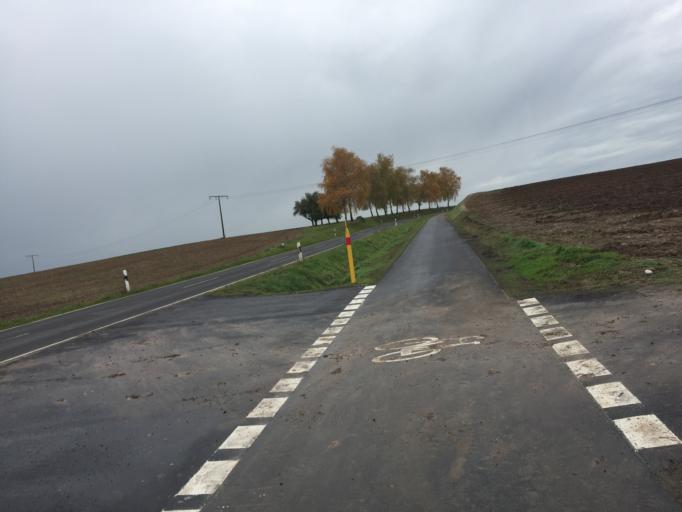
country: DE
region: Hesse
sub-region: Regierungsbezirk Giessen
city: Lich
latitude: 50.4982
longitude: 8.8253
